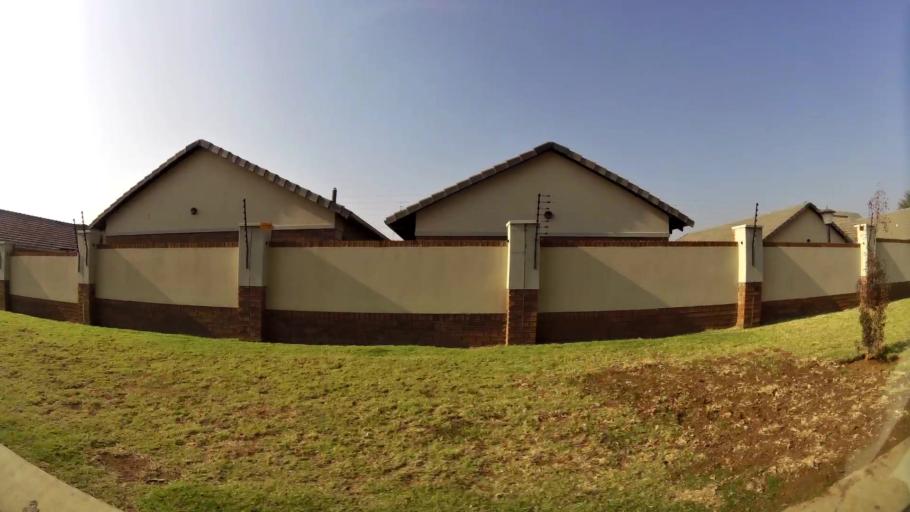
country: ZA
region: Gauteng
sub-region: City of Tshwane Metropolitan Municipality
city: Pretoria
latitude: -25.7590
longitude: 28.3273
